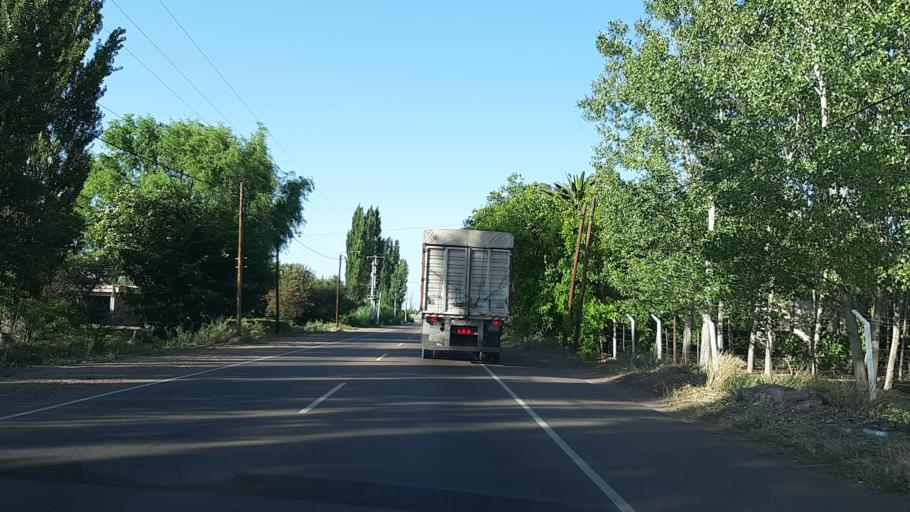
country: AR
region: Mendoza
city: San Martin
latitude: -33.0370
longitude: -68.5165
